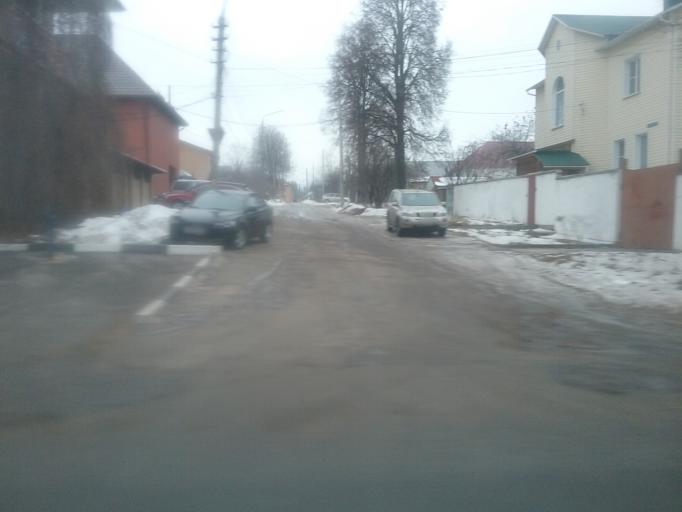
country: RU
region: Tula
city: Mendeleyevskiy
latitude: 54.1636
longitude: 37.6042
